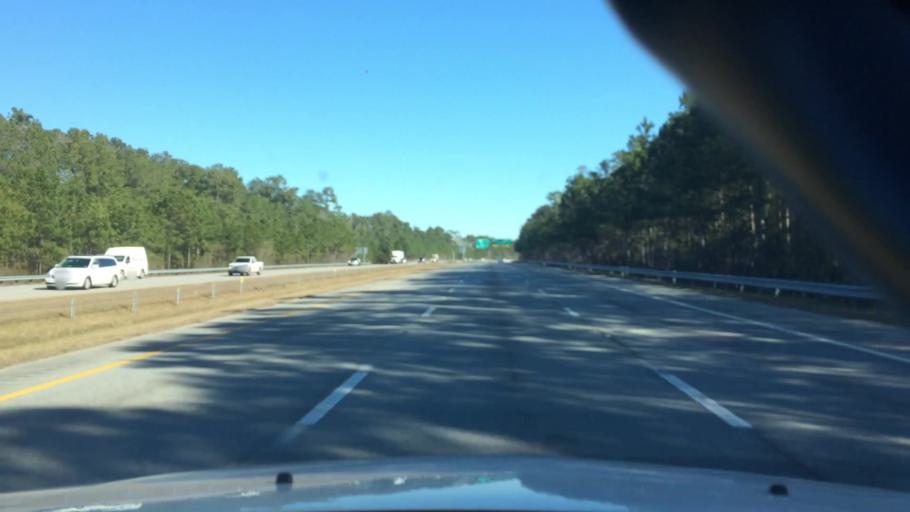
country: US
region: South Carolina
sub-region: Horry County
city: North Myrtle Beach
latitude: 33.8586
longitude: -78.6960
